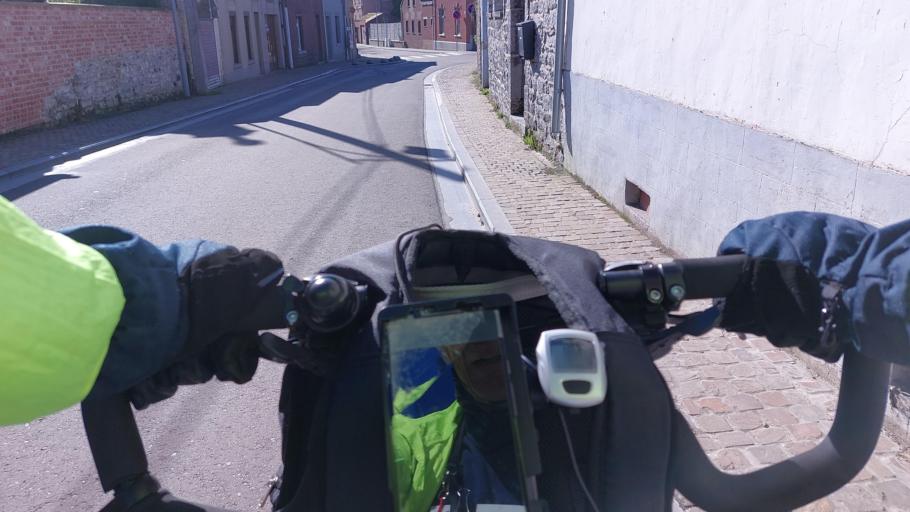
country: BE
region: Wallonia
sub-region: Province du Hainaut
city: Seneffe
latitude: 50.5620
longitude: 4.2500
